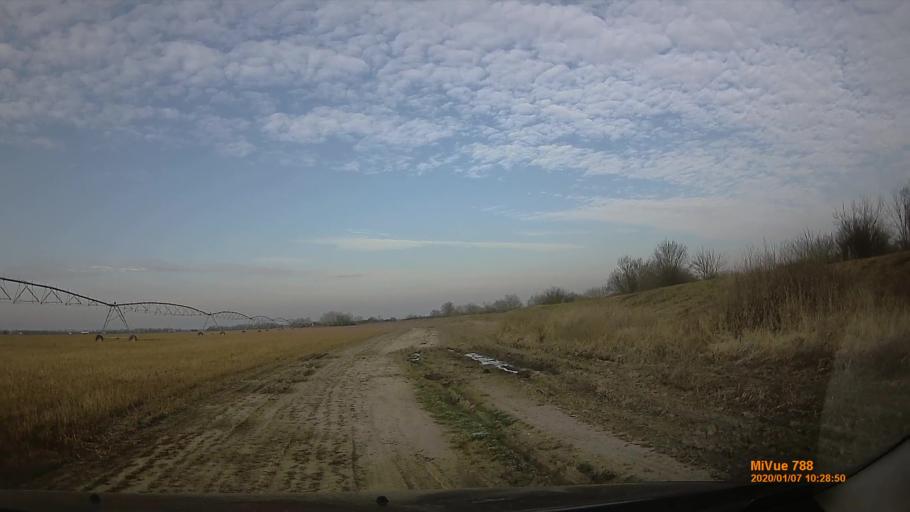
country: HU
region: Gyor-Moson-Sopron
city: Rajka
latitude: 47.9176
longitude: 17.1921
